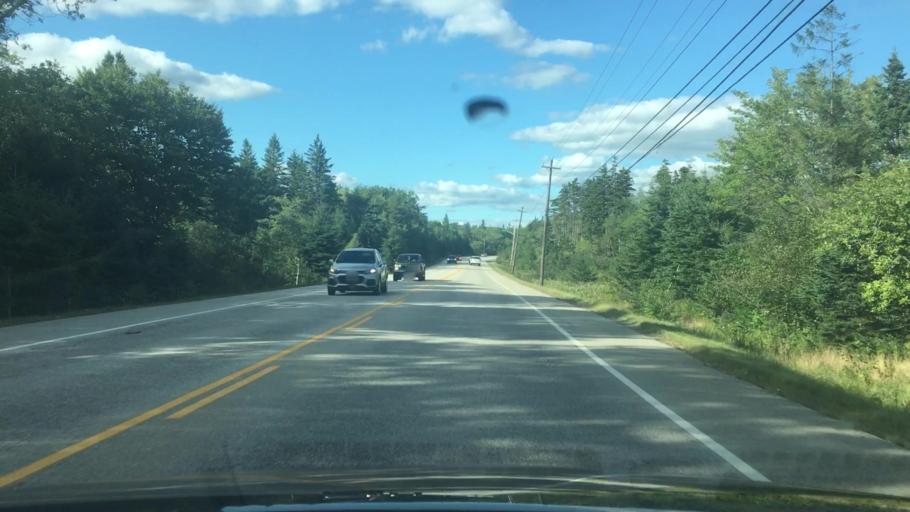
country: CA
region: Nova Scotia
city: Halifax
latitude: 44.6122
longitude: -63.6697
